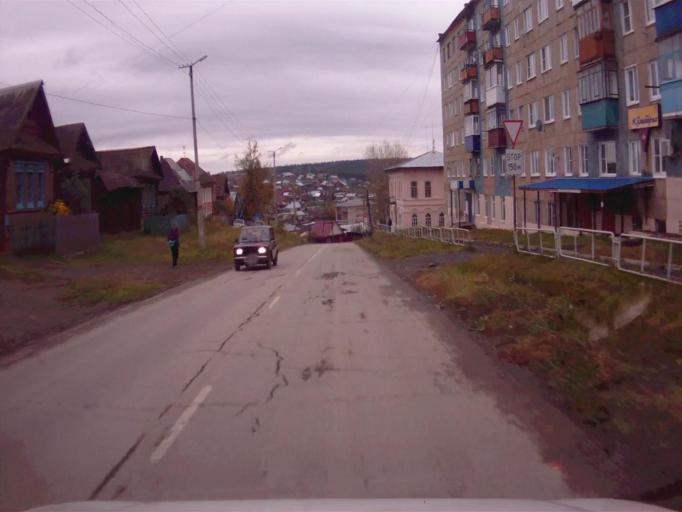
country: RU
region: Chelyabinsk
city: Nyazepetrovsk
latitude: 56.0546
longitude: 59.6040
